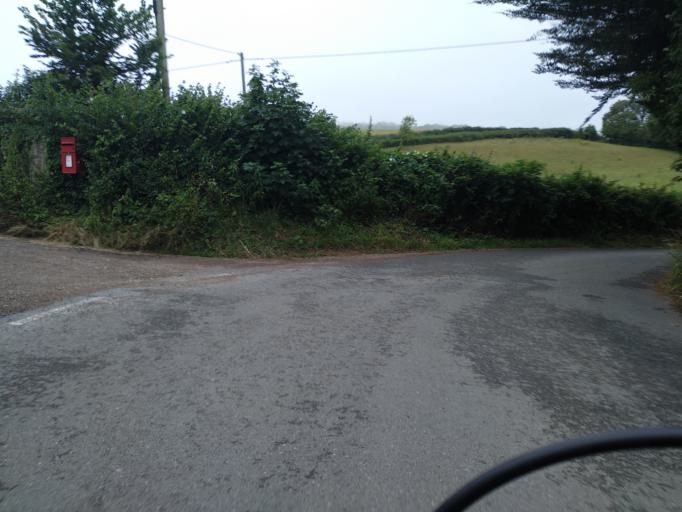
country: GB
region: England
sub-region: Isle of Wight
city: Brading
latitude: 50.6715
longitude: -1.1627
